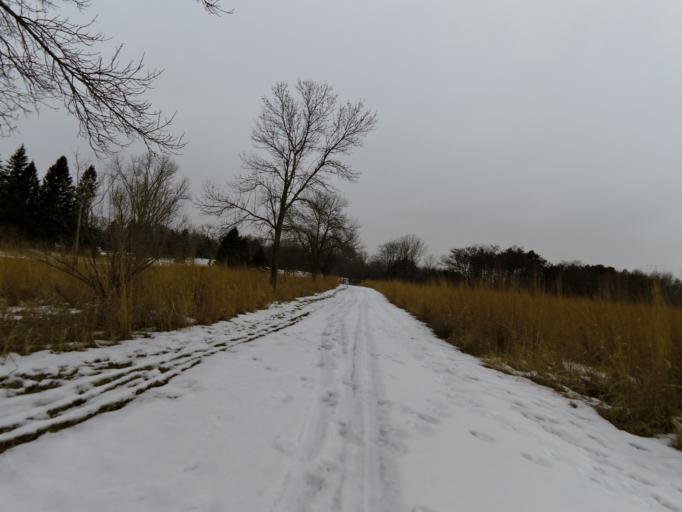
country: US
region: Wisconsin
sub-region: Pierce County
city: Prescott
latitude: 44.8027
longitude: -92.7926
